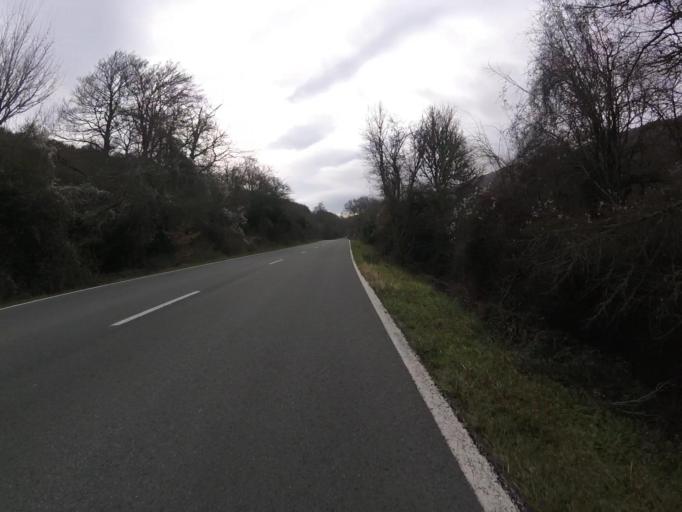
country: ES
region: Navarre
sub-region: Provincia de Navarra
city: Lezaun
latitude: 42.8316
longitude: -2.0278
